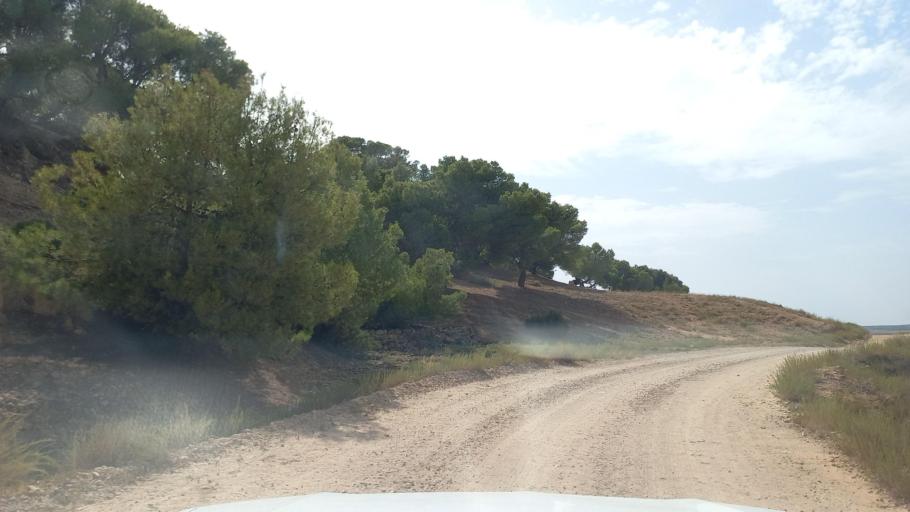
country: TN
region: Al Qasrayn
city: Kasserine
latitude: 35.3511
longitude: 8.8822
